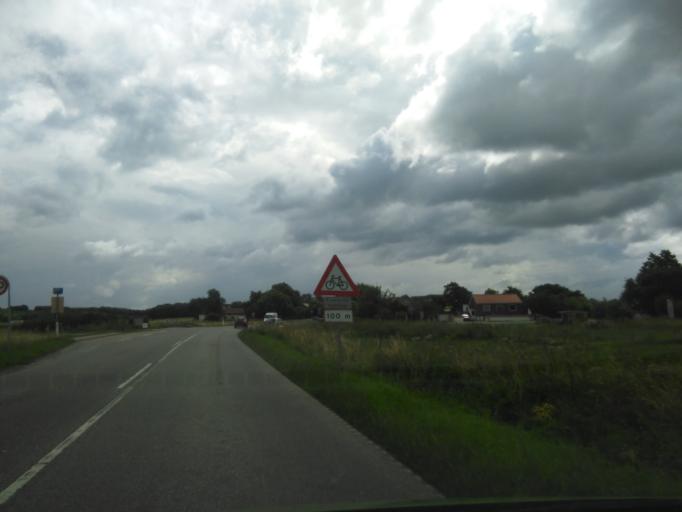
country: DK
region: Central Jutland
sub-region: Syddjurs Kommune
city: Ronde
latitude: 56.2762
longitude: 10.5064
